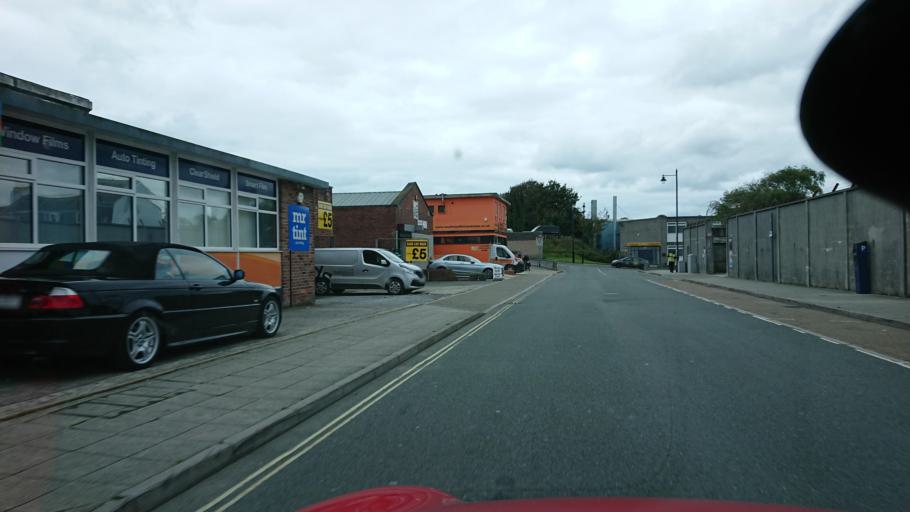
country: GB
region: England
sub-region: Plymouth
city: Plymouth
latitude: 50.3683
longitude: -4.1614
